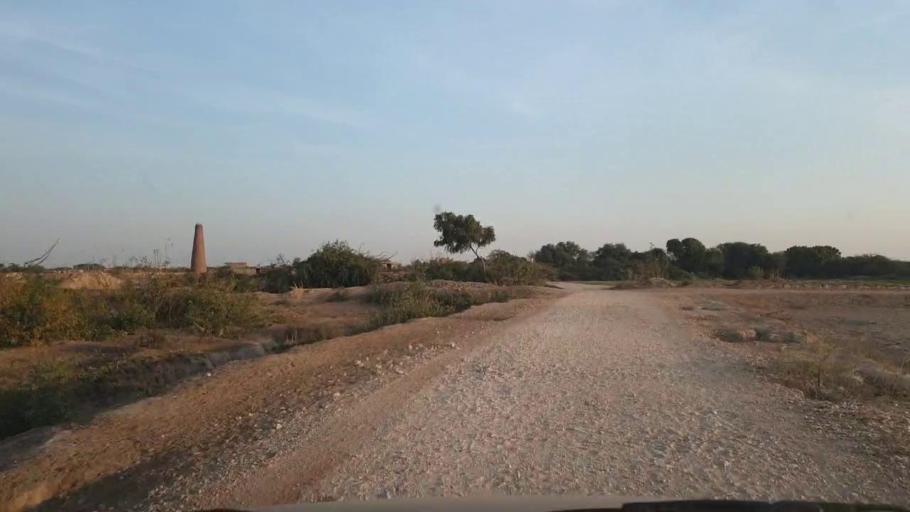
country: PK
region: Sindh
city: Chambar
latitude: 25.2810
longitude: 68.8313
